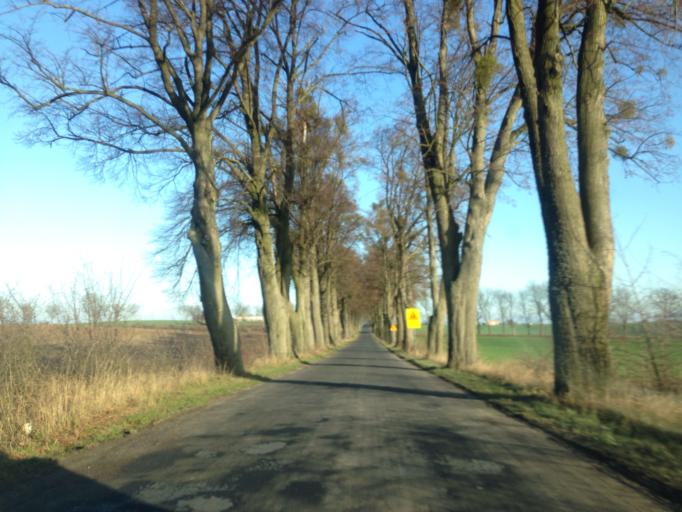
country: PL
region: Kujawsko-Pomorskie
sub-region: Powiat grudziadzki
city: Swiecie nad Osa
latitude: 53.4578
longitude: 19.1519
